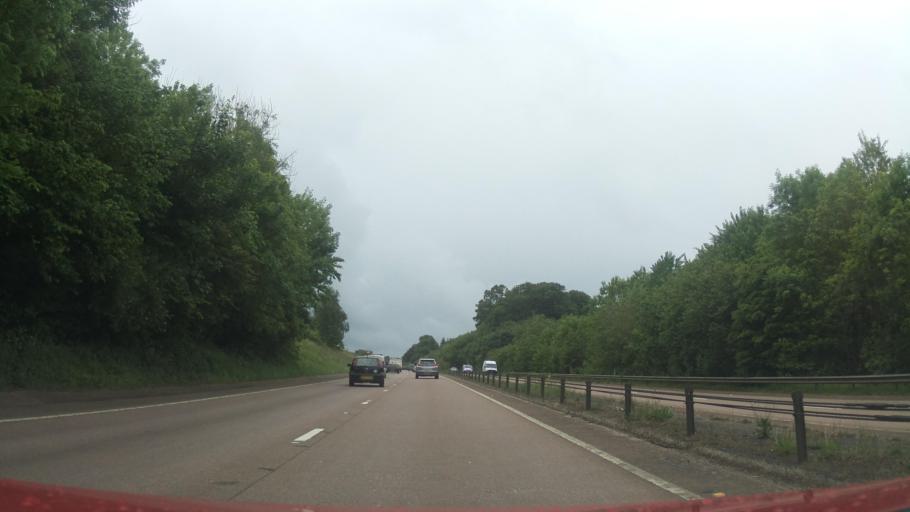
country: GB
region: England
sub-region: Devon
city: Ottery St Mary
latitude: 50.7682
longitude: -3.3040
